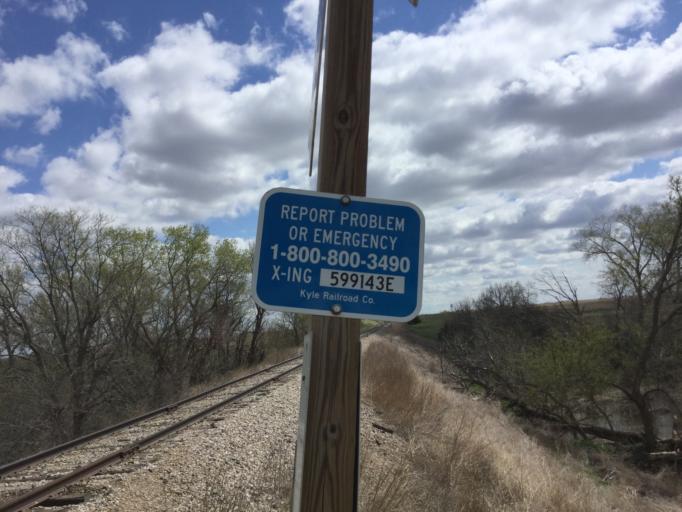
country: US
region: Kansas
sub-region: Phillips County
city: Phillipsburg
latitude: 39.7638
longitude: -99.1416
